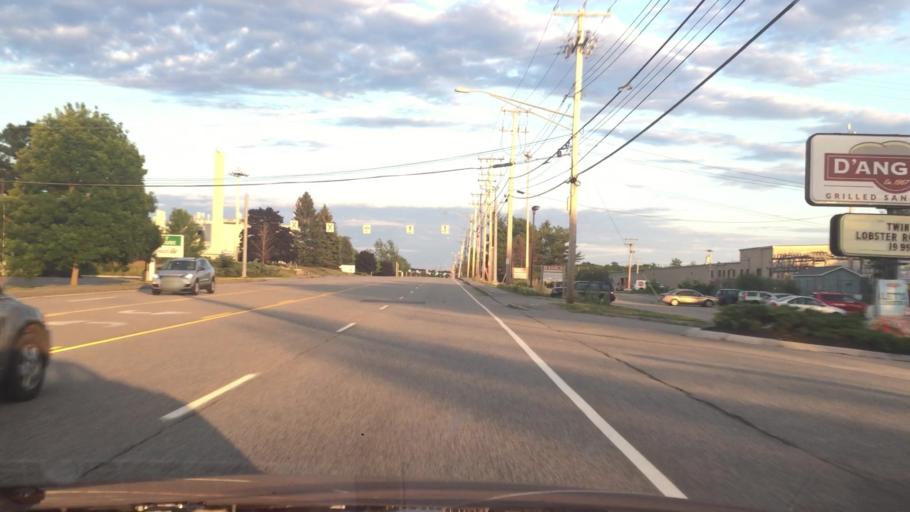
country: US
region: Maine
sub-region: Cumberland County
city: South Portland Gardens
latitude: 43.6419
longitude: -70.3287
